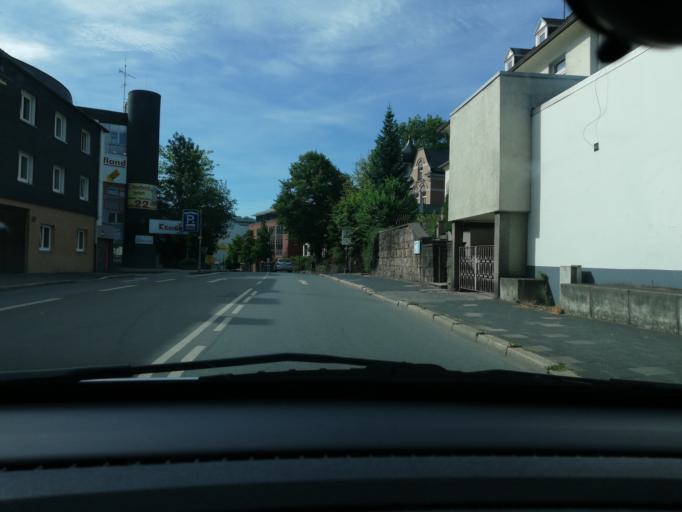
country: DE
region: North Rhine-Westphalia
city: Gevelsberg
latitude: 51.3214
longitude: 7.3381
